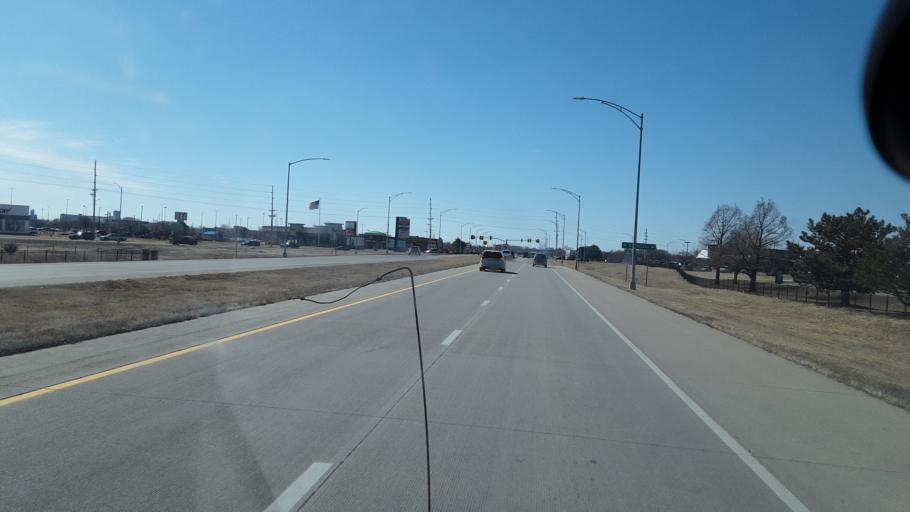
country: US
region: Kansas
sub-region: Reno County
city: Hutchinson
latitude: 38.0738
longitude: -97.8928
